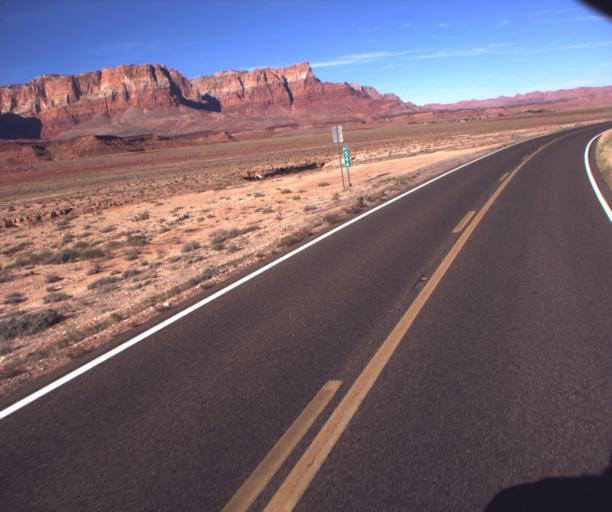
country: US
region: Arizona
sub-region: Coconino County
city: Page
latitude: 36.7644
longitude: -111.7091
